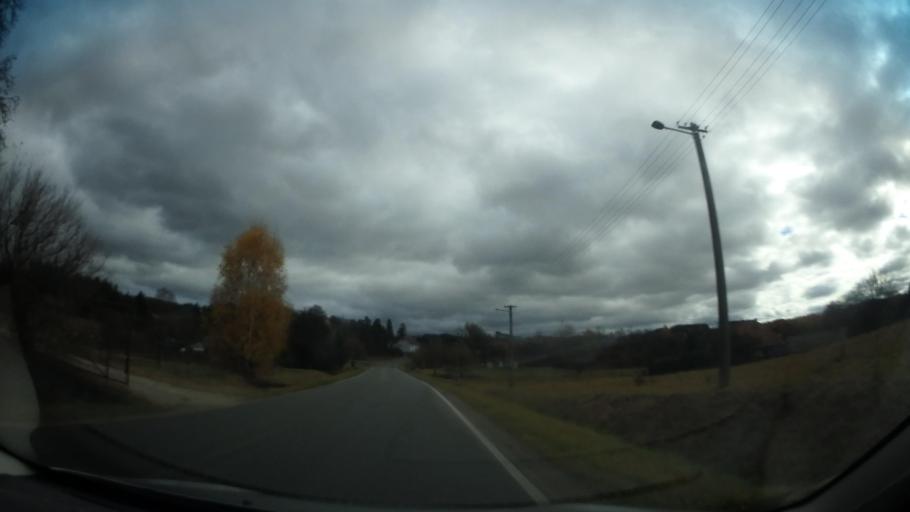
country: CZ
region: Vysocina
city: Budisov
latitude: 49.2851
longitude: 16.0996
